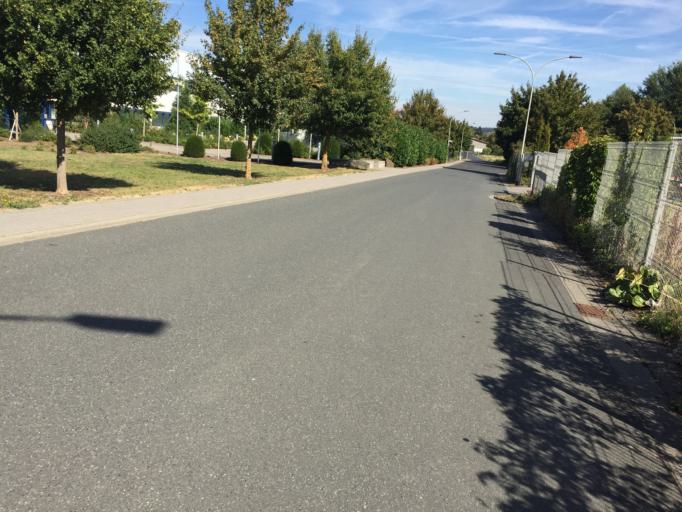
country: DE
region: Hesse
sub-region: Regierungsbezirk Giessen
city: Langgons
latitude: 50.4924
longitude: 8.6456
